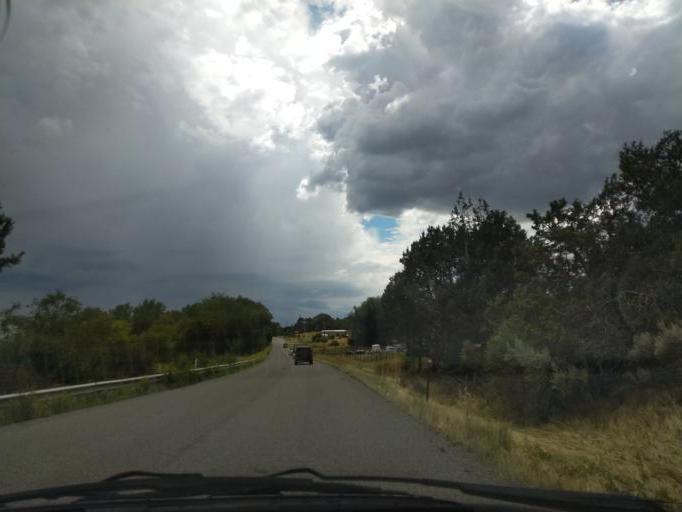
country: US
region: Colorado
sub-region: Delta County
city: Paonia
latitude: 38.8920
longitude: -107.5791
